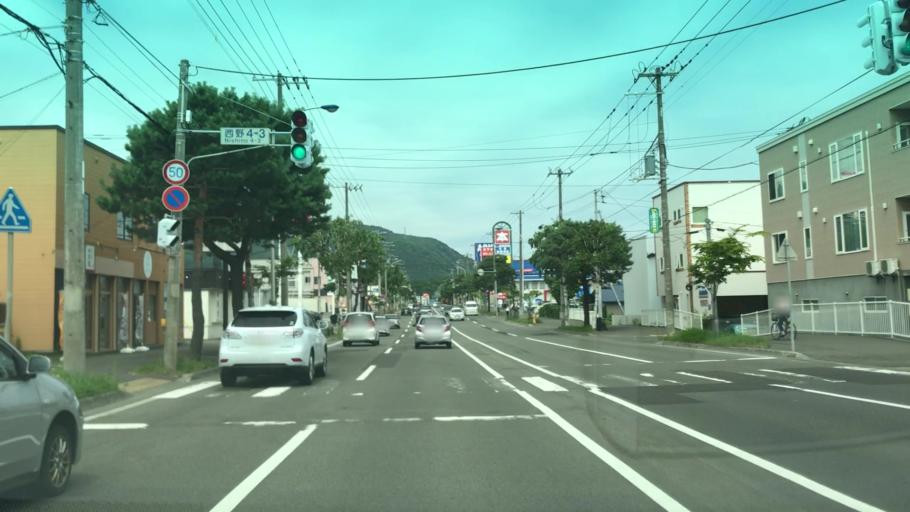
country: JP
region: Hokkaido
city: Sapporo
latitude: 43.0738
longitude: 141.2791
